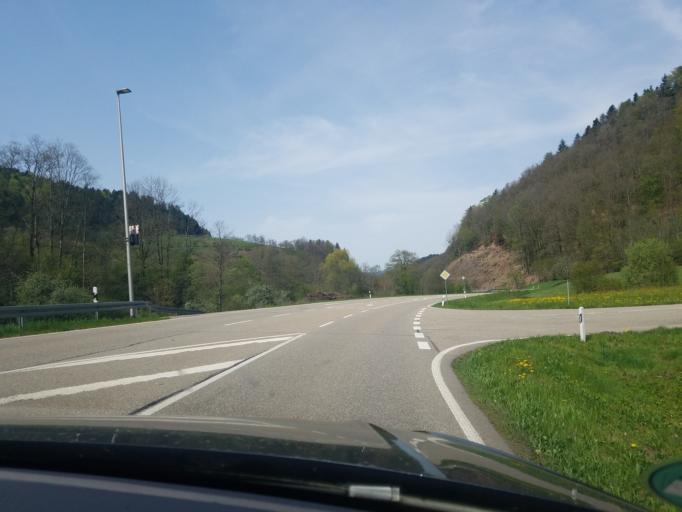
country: DE
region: Baden-Wuerttemberg
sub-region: Freiburg Region
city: Oppenau
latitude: 48.4372
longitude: 8.1721
